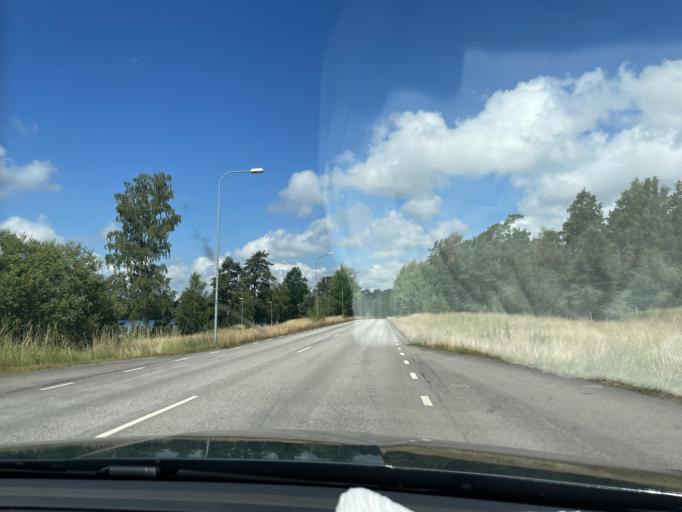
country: SE
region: Kronoberg
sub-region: Vaxjo Kommun
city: Vaexjoe
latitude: 56.8625
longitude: 14.8381
